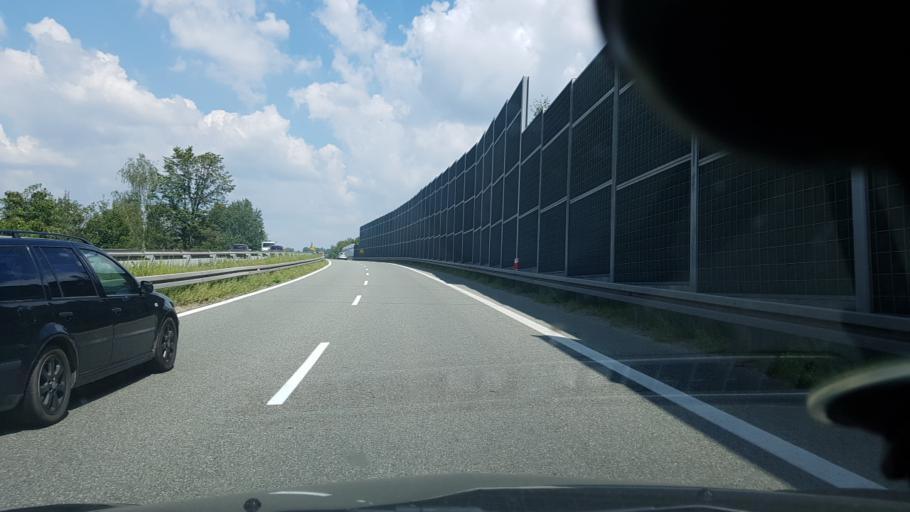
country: PL
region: Silesian Voivodeship
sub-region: Powiat mikolowski
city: Laziska Gorne
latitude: 50.1313
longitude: 18.8279
